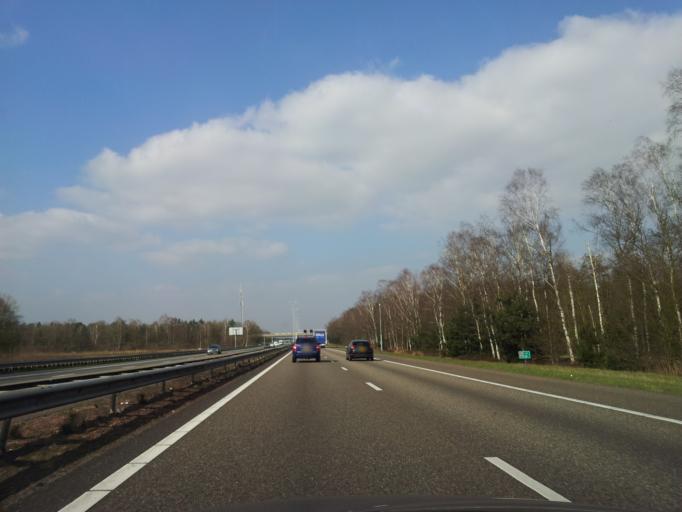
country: NL
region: North Brabant
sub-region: Gemeente Eindhoven
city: De Doornakkers
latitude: 51.3892
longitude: 5.5093
